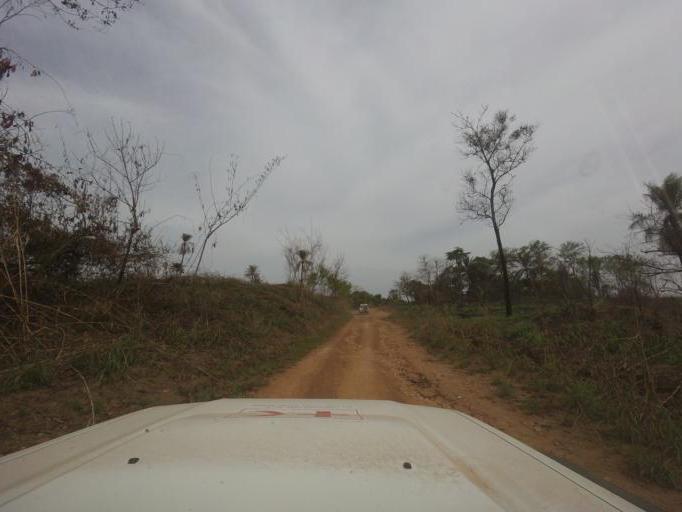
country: GN
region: Nzerekore
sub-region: Prefecture de Guekedou
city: Gueckedou
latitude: 8.4478
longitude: -10.2483
